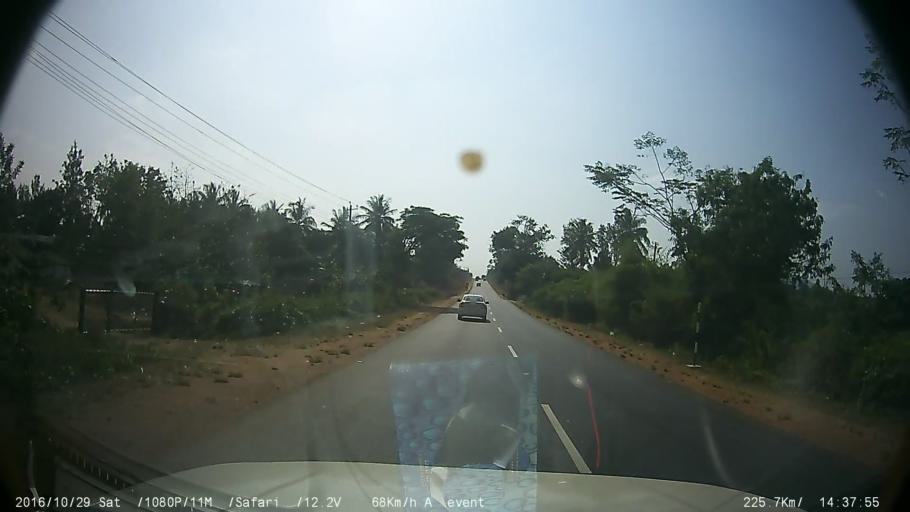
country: IN
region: Karnataka
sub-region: Kodagu
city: Kushalnagar
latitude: 12.4436
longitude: 75.9221
